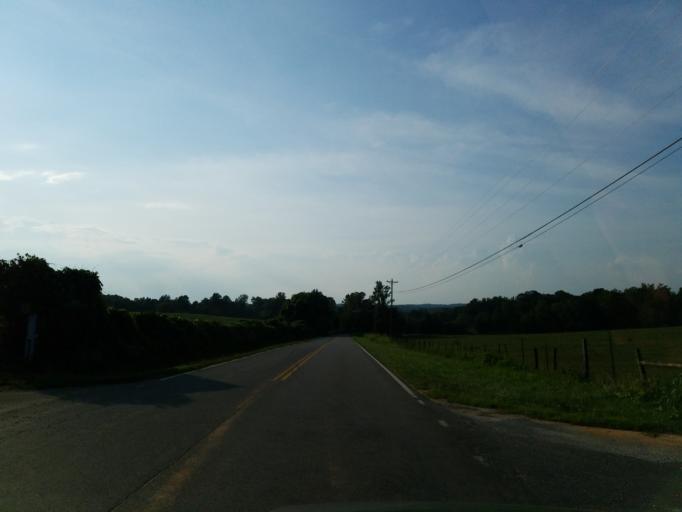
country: US
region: Georgia
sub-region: Pickens County
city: Jasper
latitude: 34.5377
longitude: -84.5341
